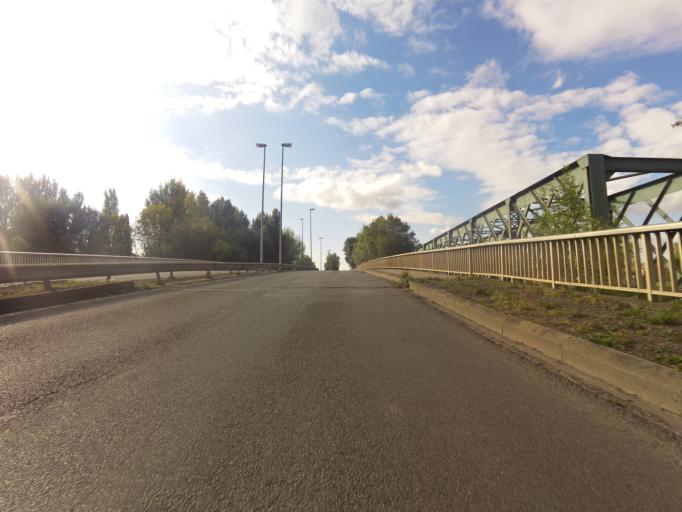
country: FR
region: Nord-Pas-de-Calais
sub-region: Departement du Nord
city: Neuville-Saint-Remy
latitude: 50.1742
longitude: 3.2214
